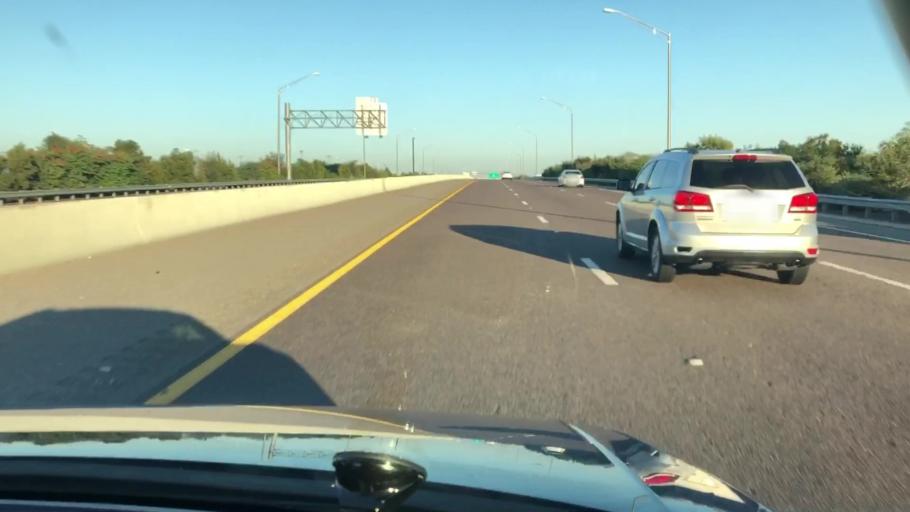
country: US
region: Florida
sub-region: Orange County
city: Clarcona
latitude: 28.6341
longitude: -81.4790
